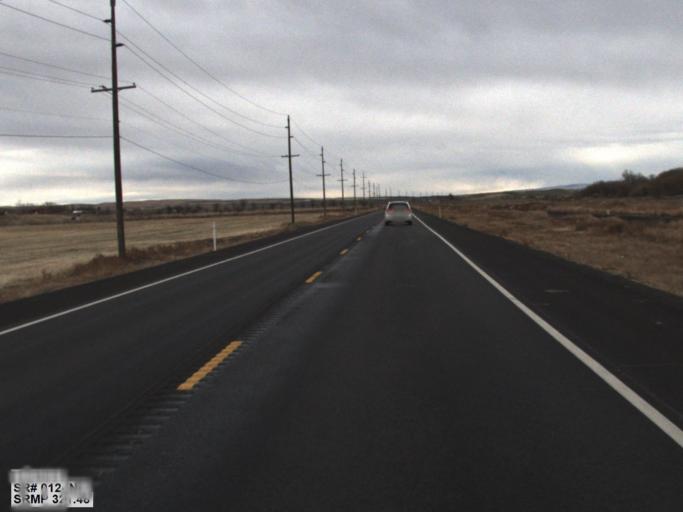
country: US
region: Washington
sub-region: Walla Walla County
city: Garrett
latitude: 46.0448
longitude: -118.6422
